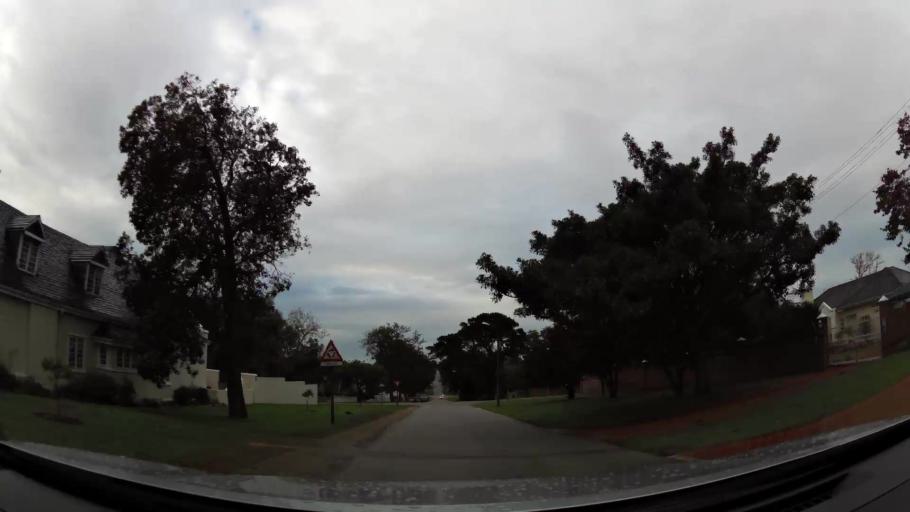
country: ZA
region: Eastern Cape
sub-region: Nelson Mandela Bay Metropolitan Municipality
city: Port Elizabeth
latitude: -33.9762
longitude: 25.5812
